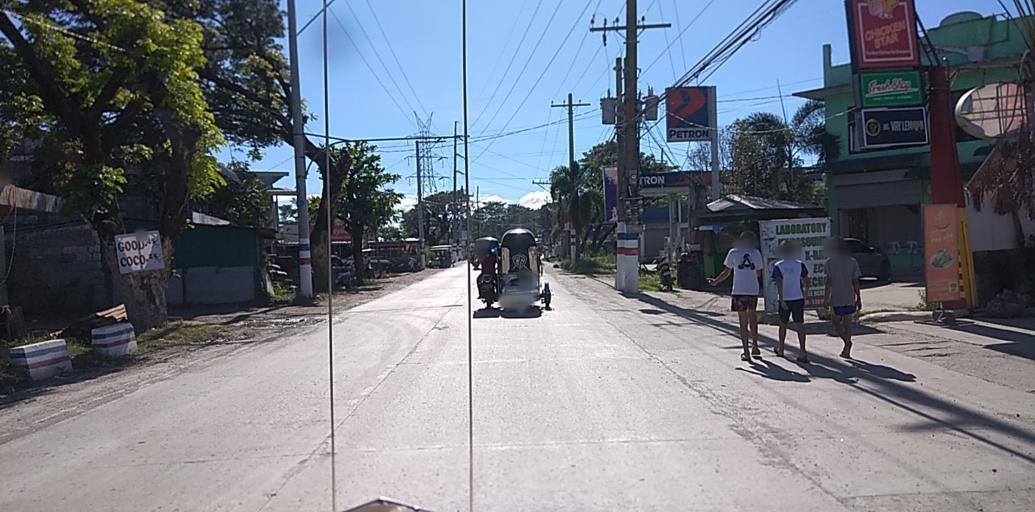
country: PH
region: Central Luzon
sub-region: Province of Pampanga
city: San Luis
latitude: 15.0437
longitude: 120.7889
